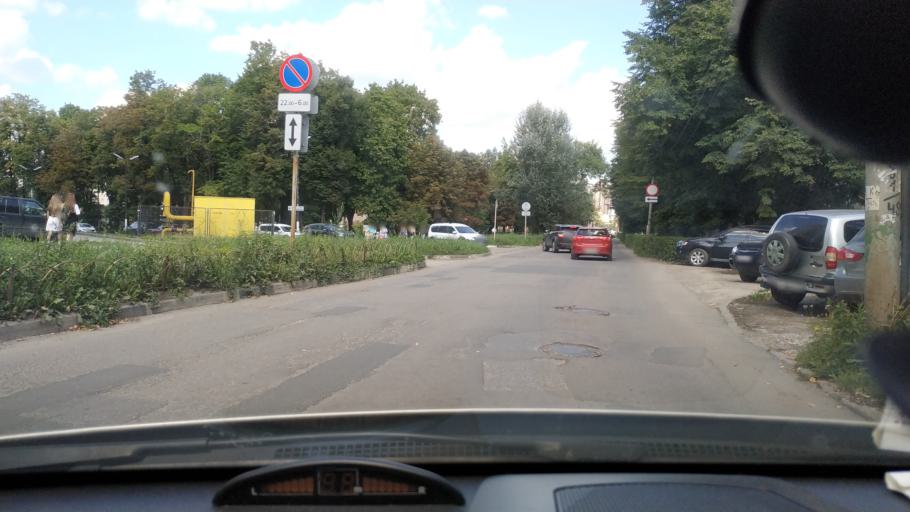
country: RU
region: Rjazan
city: Ryazan'
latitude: 54.6242
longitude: 39.7107
